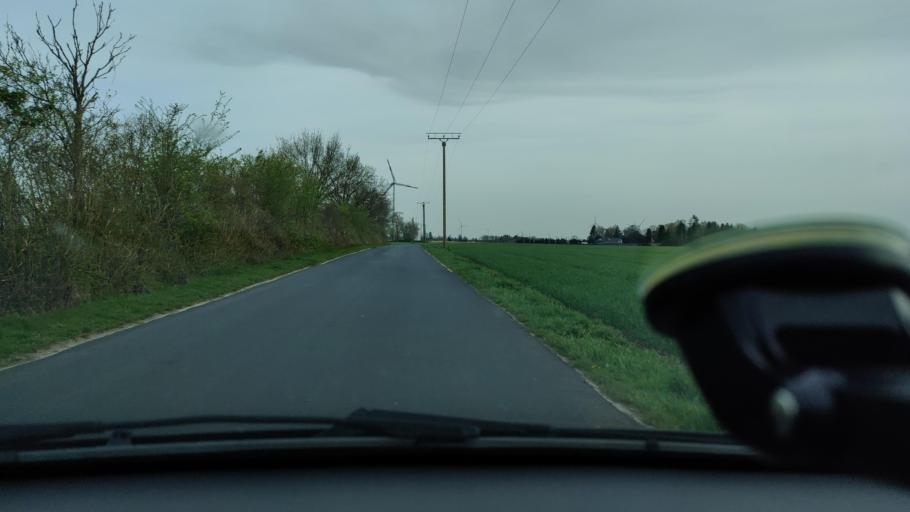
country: DE
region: North Rhine-Westphalia
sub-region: Regierungsbezirk Dusseldorf
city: Goch
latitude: 51.7323
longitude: 6.1953
